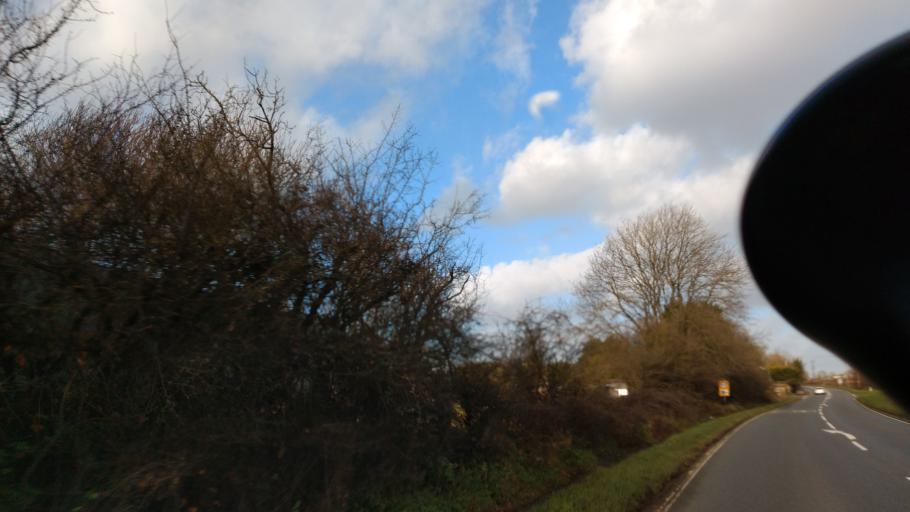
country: GB
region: England
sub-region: Somerset
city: Shepton Mallet
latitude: 51.1534
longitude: -2.5442
